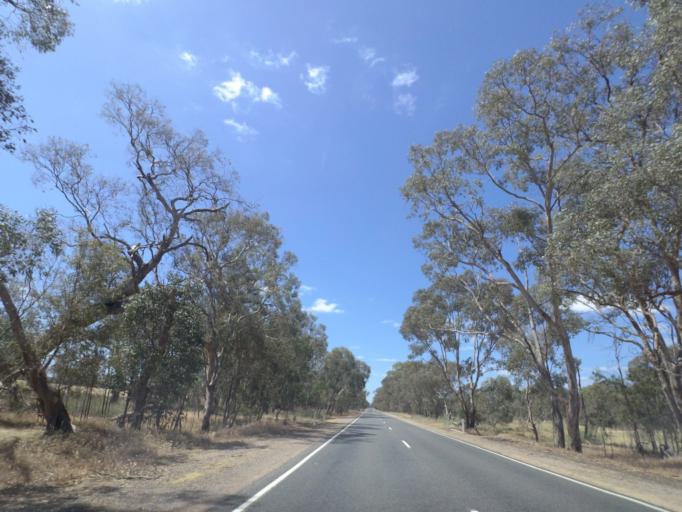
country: AU
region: Victoria
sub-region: Wangaratta
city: Wangaratta
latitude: -36.4340
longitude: 146.2511
